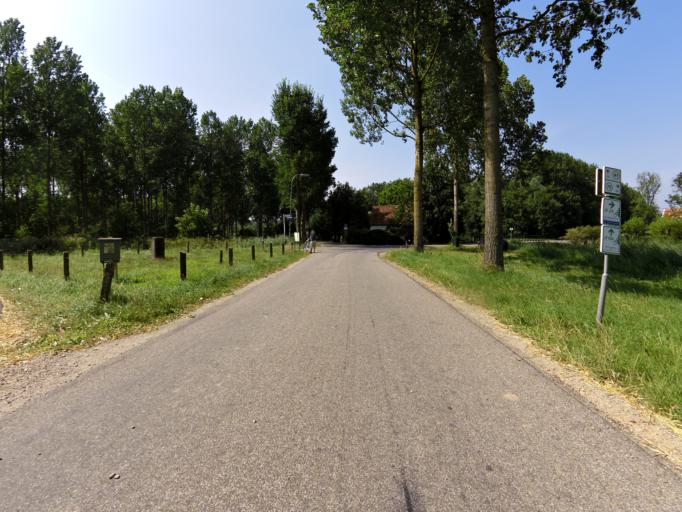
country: NL
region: South Holland
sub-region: Gemeente Dordrecht
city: Dordrecht
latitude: 51.7605
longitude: 4.6952
